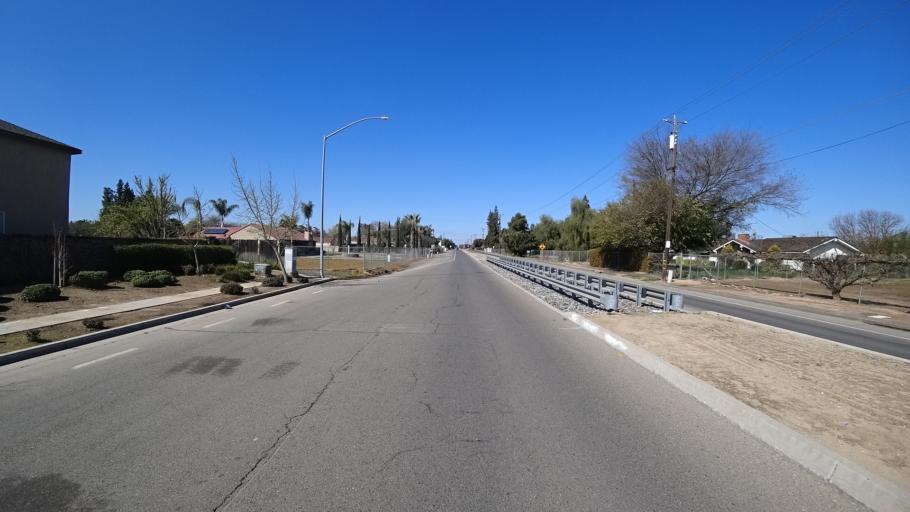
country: US
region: California
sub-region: Fresno County
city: West Park
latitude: 36.7645
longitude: -119.8778
